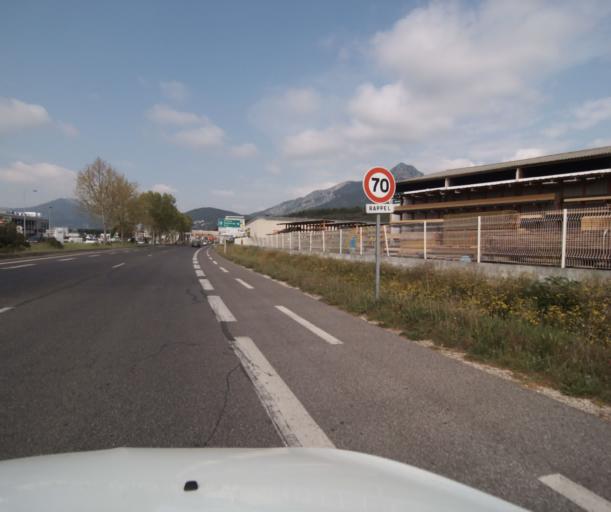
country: FR
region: Provence-Alpes-Cote d'Azur
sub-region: Departement du Var
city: La Garde
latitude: 43.1366
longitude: 6.0289
